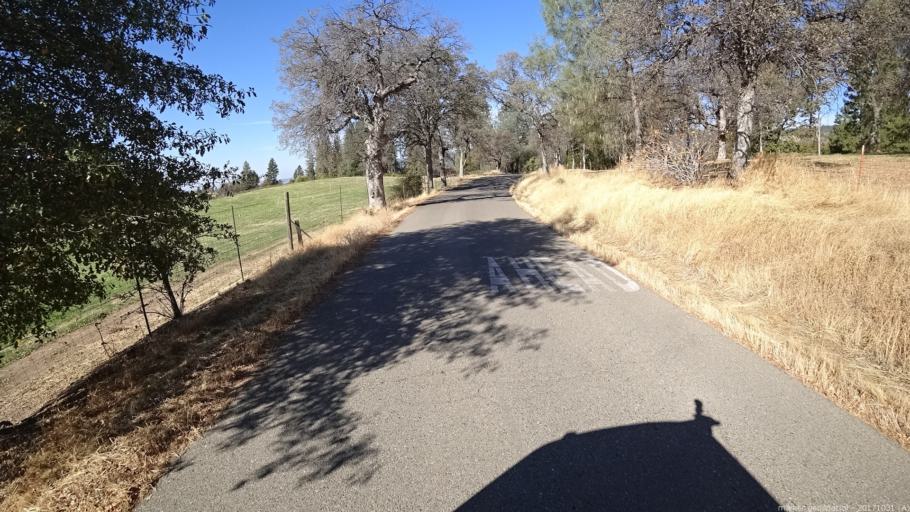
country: US
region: California
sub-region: Shasta County
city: Shingletown
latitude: 40.4455
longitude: -121.8384
